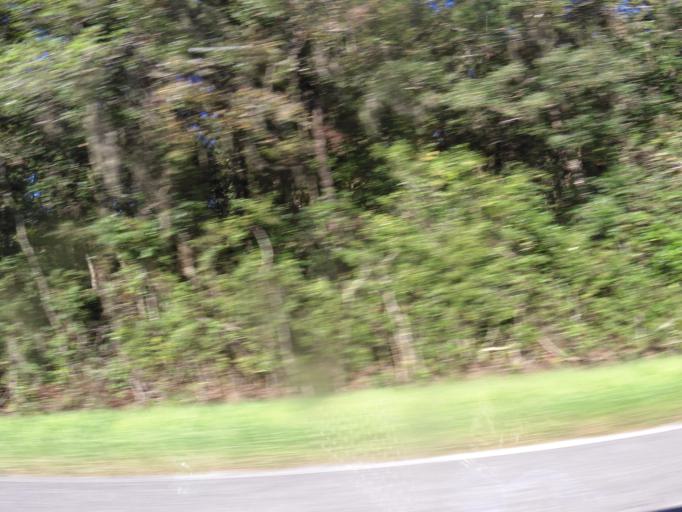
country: US
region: Florida
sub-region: Putnam County
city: East Palatka
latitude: 29.7855
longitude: -81.4944
